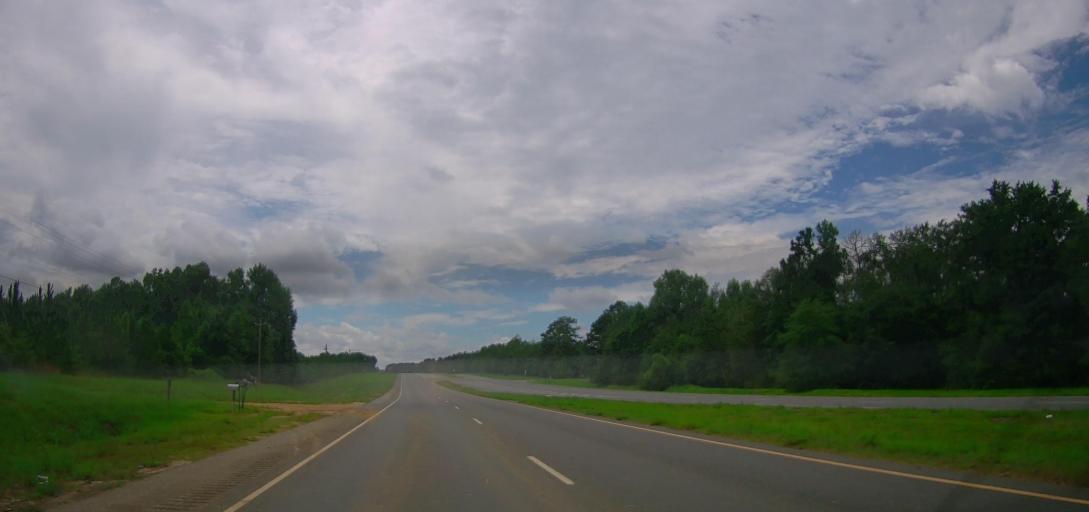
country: US
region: Georgia
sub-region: Telfair County
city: Helena
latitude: 32.1053
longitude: -82.9788
